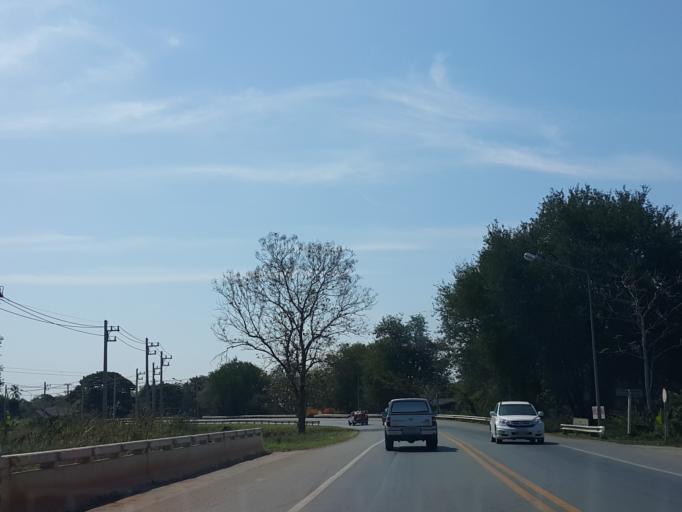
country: TH
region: Sukhothai
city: Sawankhalok
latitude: 17.2729
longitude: 99.8407
